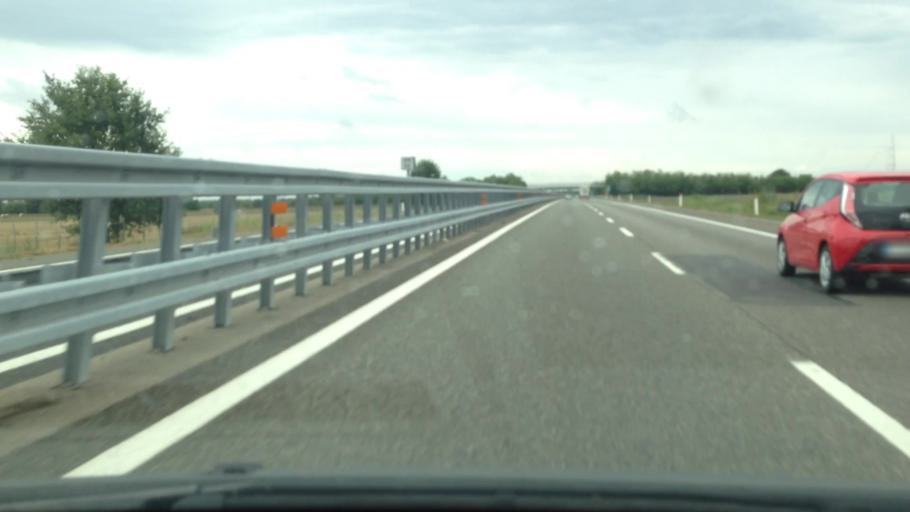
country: IT
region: Piedmont
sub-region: Provincia di Alessandria
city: Felizzano
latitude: 44.9191
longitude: 8.4572
